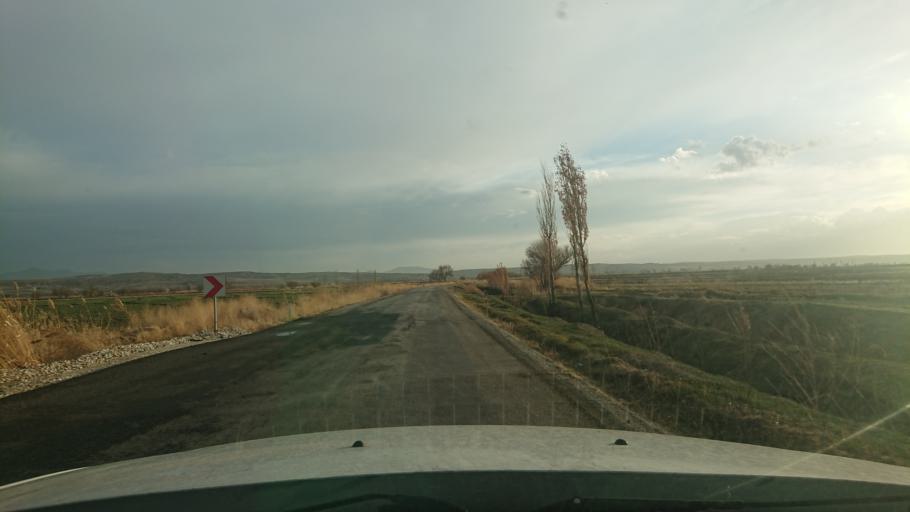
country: TR
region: Aksaray
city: Acipinar
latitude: 38.4748
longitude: 33.8598
